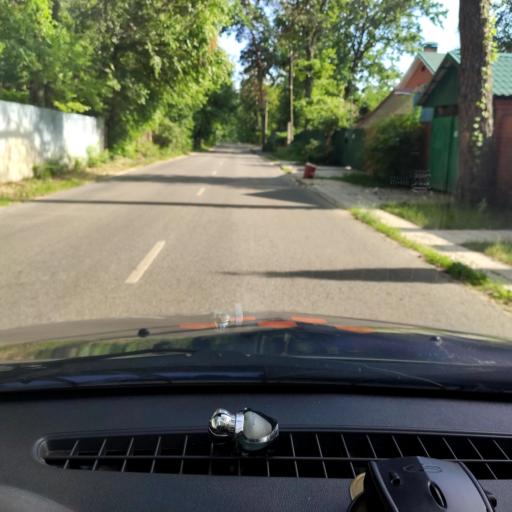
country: RU
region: Voronezj
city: Somovo
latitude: 51.7529
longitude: 39.3660
